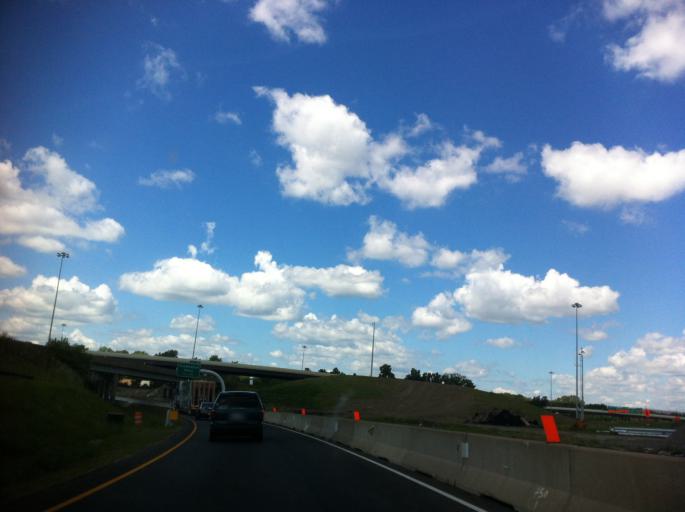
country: US
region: Ohio
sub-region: Lucas County
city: Toledo
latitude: 41.6739
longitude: -83.5730
